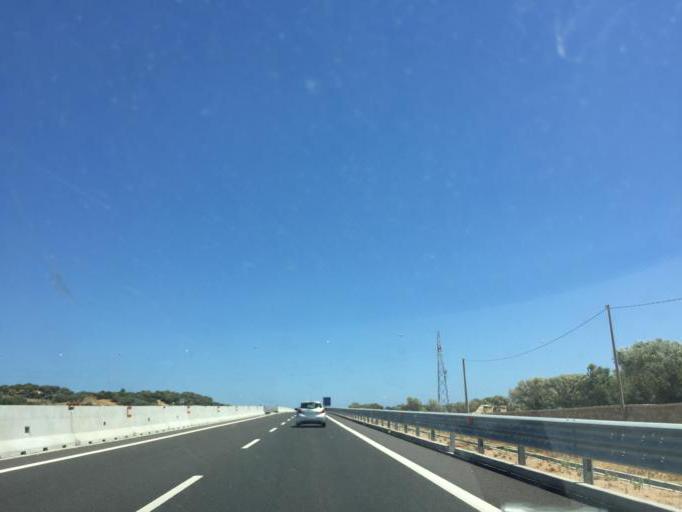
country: IT
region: Sardinia
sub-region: Provincia di Olbia-Tempio
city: Loiri Porto San Paolo
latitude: 40.8837
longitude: 9.4716
